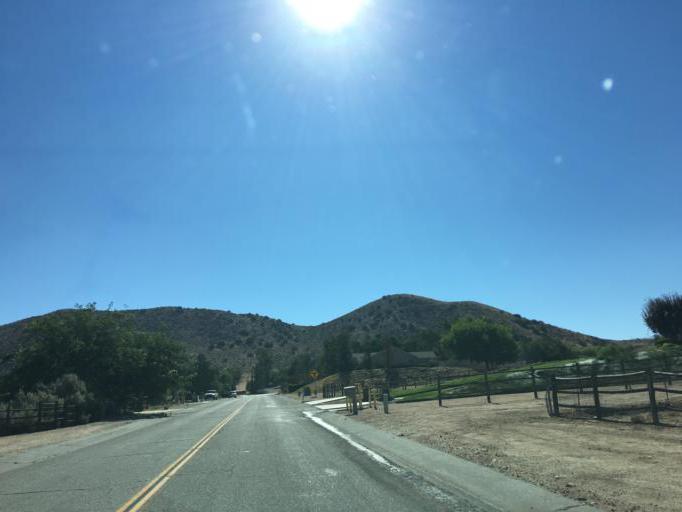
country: US
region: California
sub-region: Los Angeles County
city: Acton
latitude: 34.4646
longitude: -118.1697
